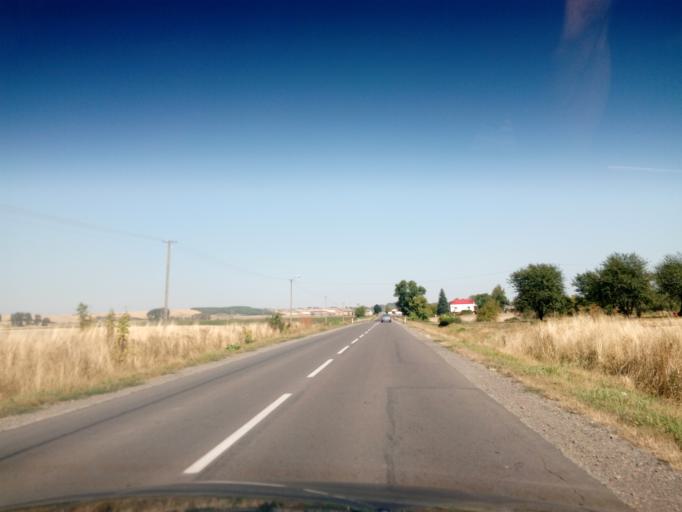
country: PL
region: Lublin Voivodeship
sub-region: Powiat hrubieszowski
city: Horodlo
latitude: 50.8381
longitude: 23.9855
